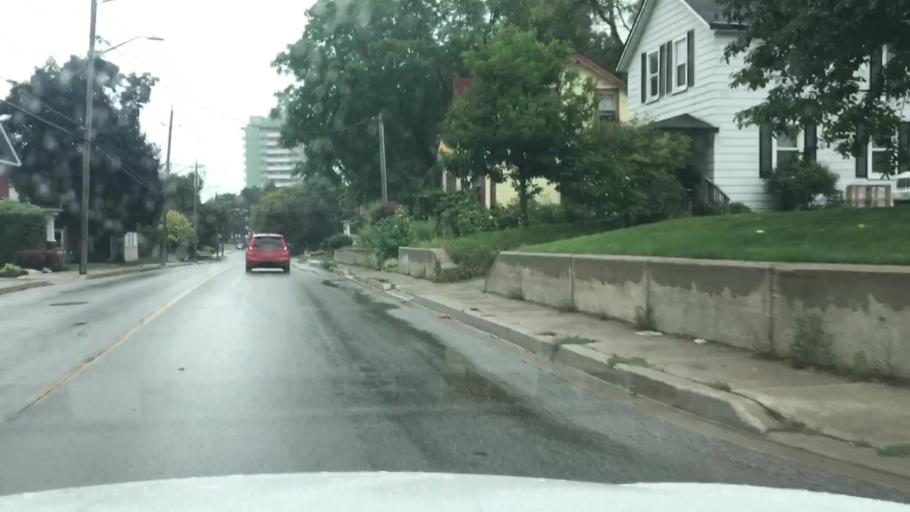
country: CA
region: Ontario
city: Newmarket
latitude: 44.0494
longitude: -79.4600
